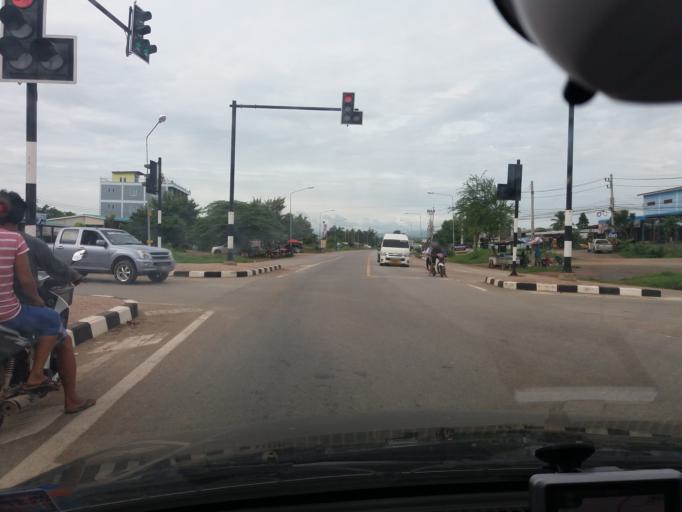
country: TH
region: Kanchanaburi
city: Dan Makham Tia
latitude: 13.9489
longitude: 99.2905
